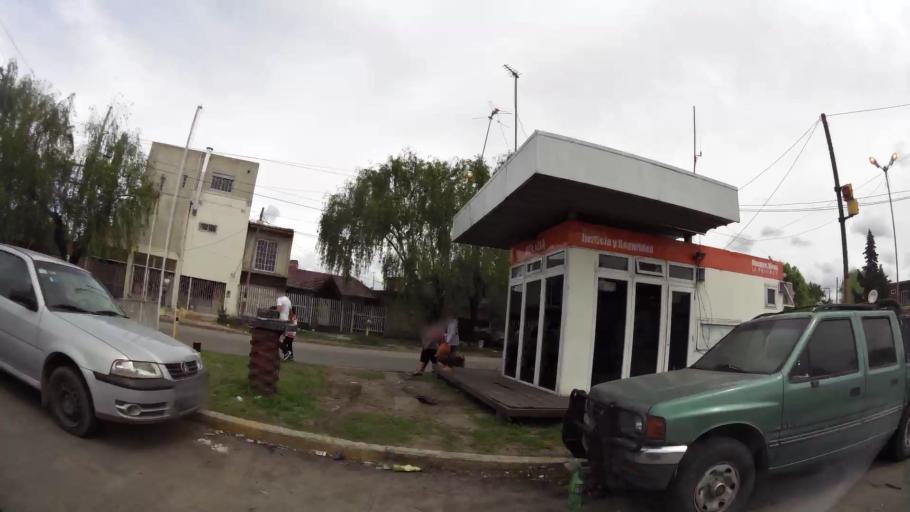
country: AR
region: Buenos Aires
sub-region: Partido de Quilmes
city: Quilmes
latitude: -34.7597
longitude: -58.2555
